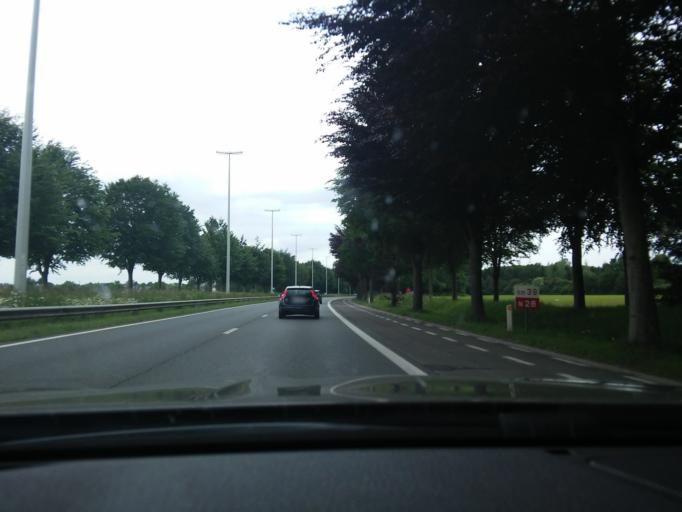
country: BE
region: Flanders
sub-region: Provincie Oost-Vlaanderen
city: Ninove
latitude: 50.8482
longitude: 4.0275
